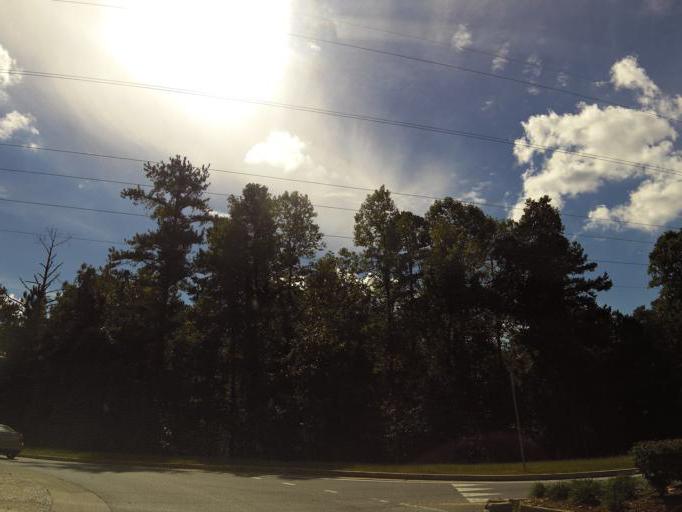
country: US
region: Georgia
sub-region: Pickens County
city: Nelson
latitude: 34.4273
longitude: -84.2762
